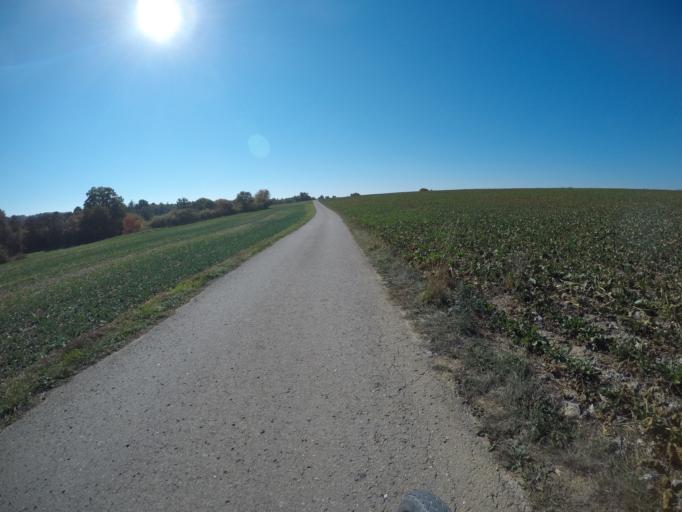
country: DE
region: Baden-Wuerttemberg
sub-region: Regierungsbezirk Stuttgart
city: Bondorf
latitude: 48.5388
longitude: 8.8814
